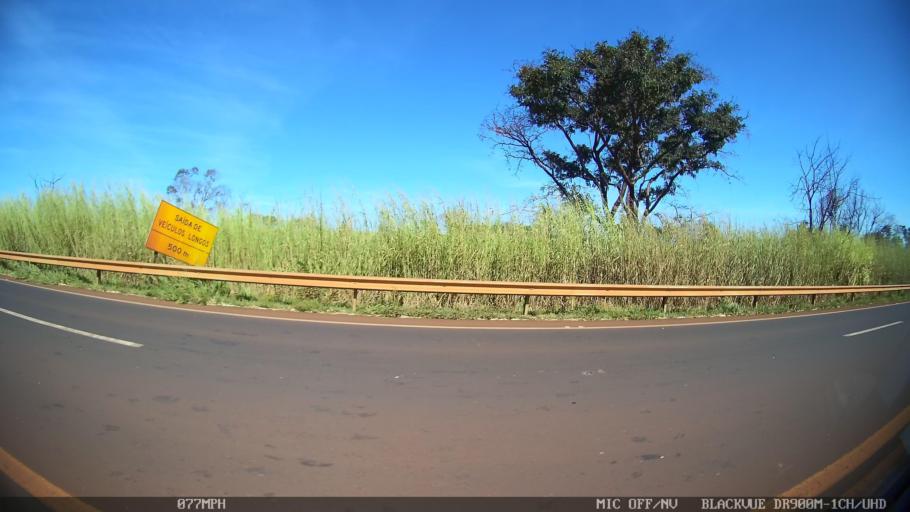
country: BR
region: Sao Paulo
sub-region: Sao Joaquim Da Barra
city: Sao Joaquim da Barra
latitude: -20.5473
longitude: -47.7661
